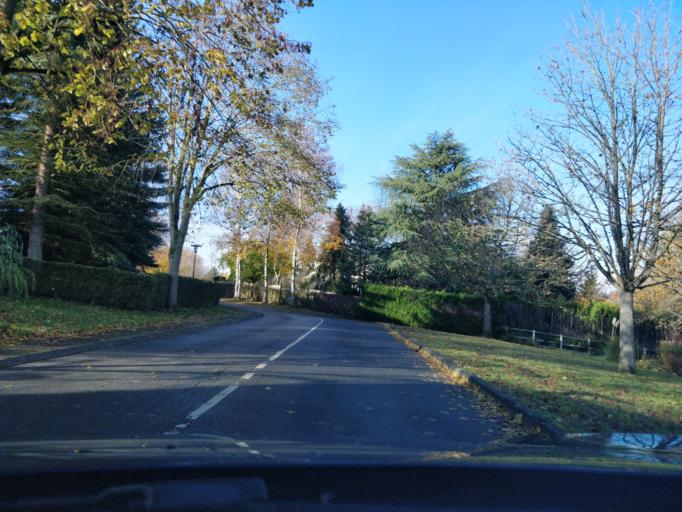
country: FR
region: Ile-de-France
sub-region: Departement de l'Essonne
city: Limours
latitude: 48.6384
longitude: 2.0869
